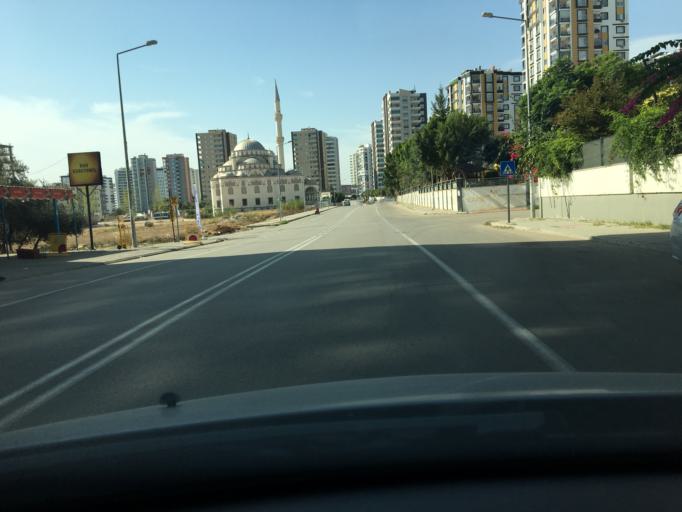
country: TR
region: Adana
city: Seyhan
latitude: 37.0195
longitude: 35.2612
